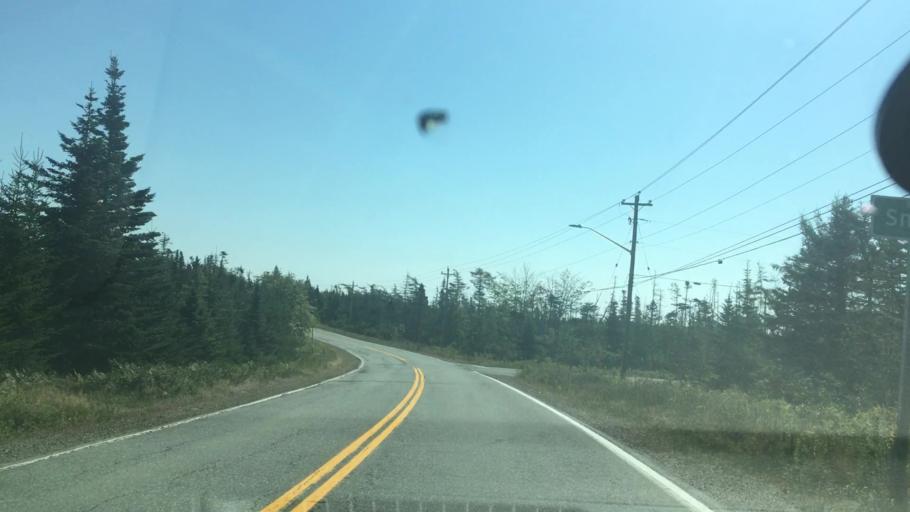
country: CA
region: Nova Scotia
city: New Glasgow
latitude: 44.9186
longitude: -62.3336
